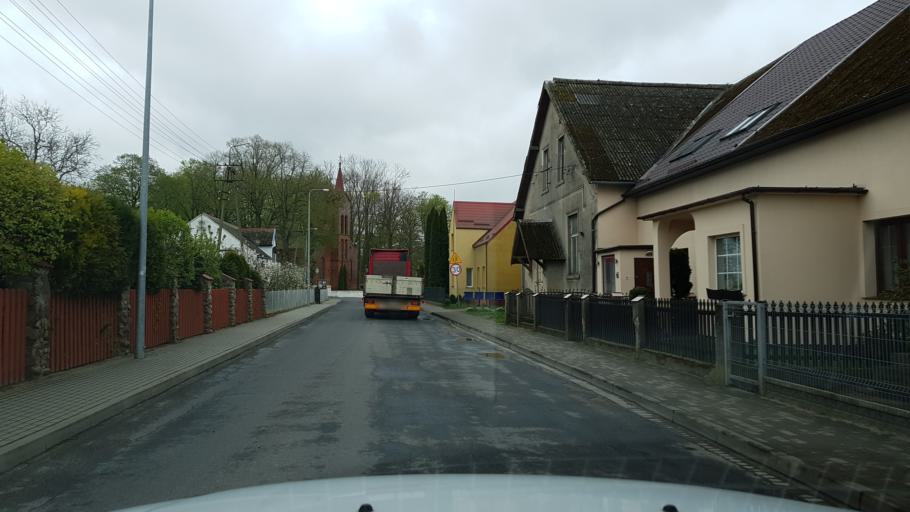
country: PL
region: West Pomeranian Voivodeship
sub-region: Powiat kolobrzeski
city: Ryman
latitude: 54.0284
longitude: 15.5307
